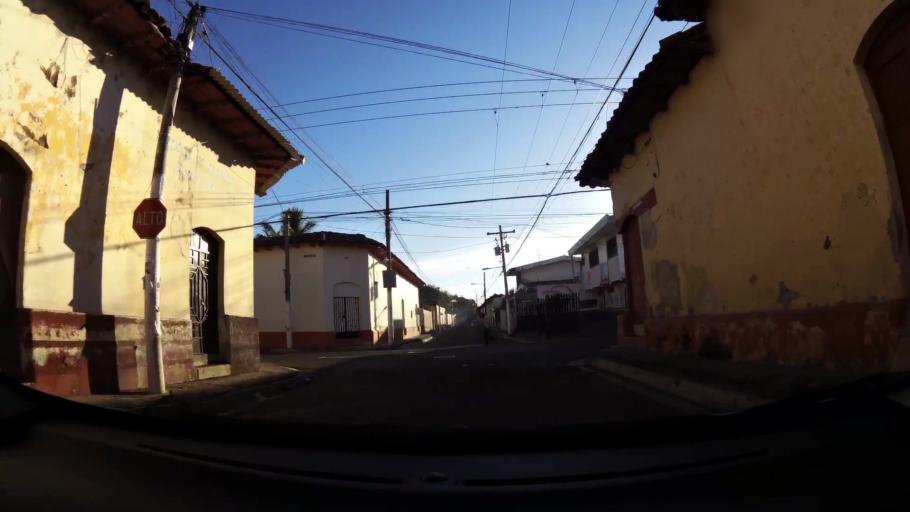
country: SV
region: San Miguel
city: San Miguel
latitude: 13.4869
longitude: -88.1754
